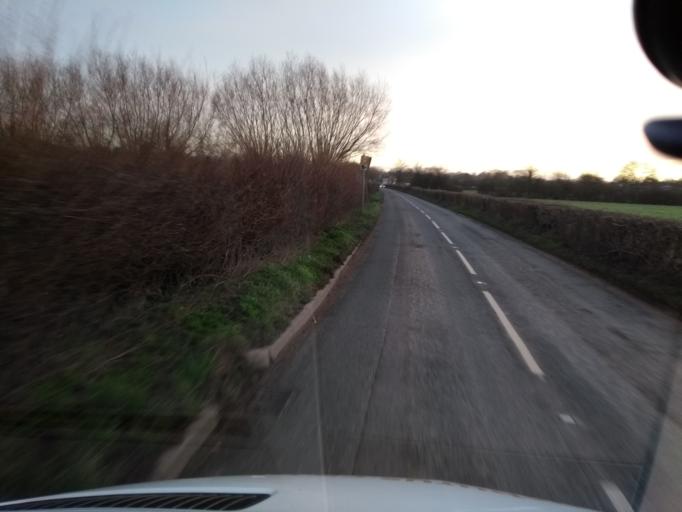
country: GB
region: England
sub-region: Somerset
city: Wedmore
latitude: 51.2227
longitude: -2.8254
